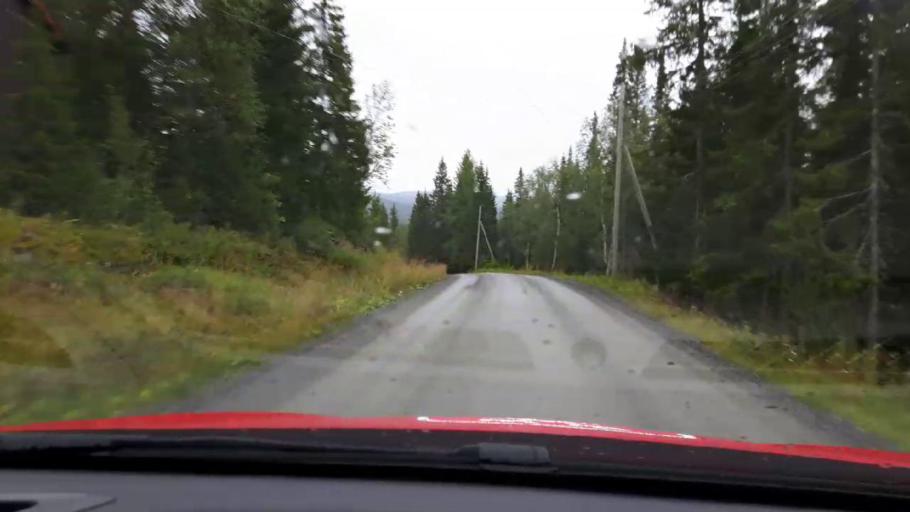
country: SE
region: Jaemtland
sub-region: Are Kommun
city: Are
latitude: 63.5070
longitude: 12.7289
